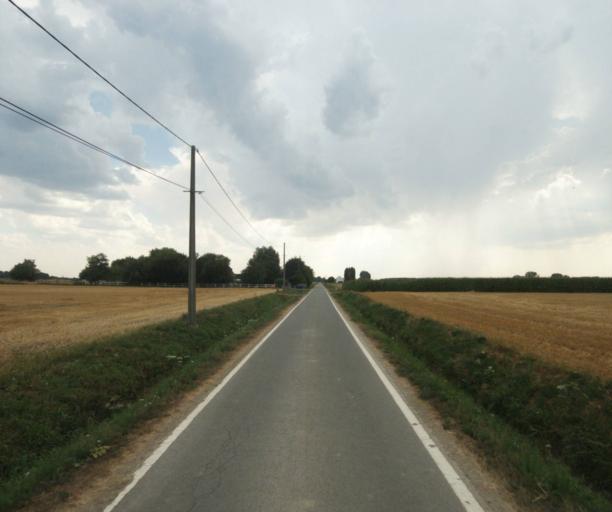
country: FR
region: Nord-Pas-de-Calais
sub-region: Departement du Nord
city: Deulemont
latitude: 50.7342
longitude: 2.9652
